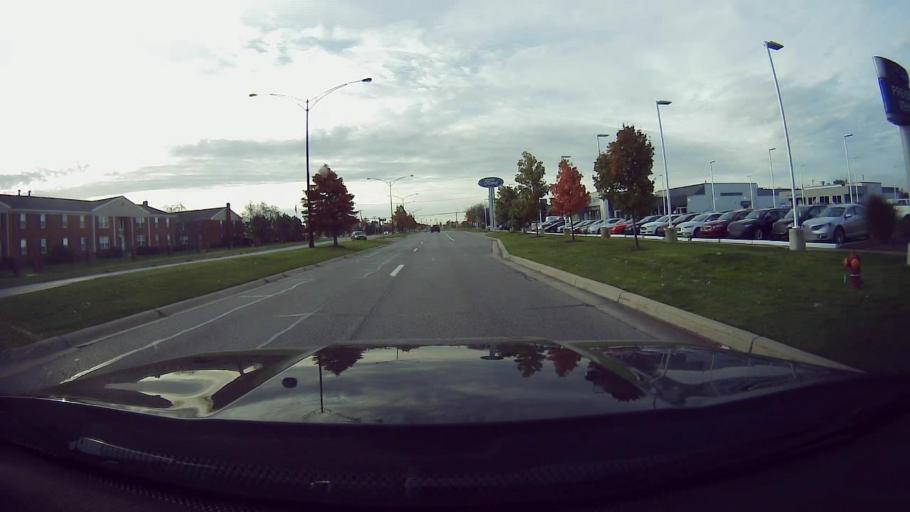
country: US
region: Michigan
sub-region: Oakland County
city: Clawson
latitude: 42.5437
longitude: -83.1076
